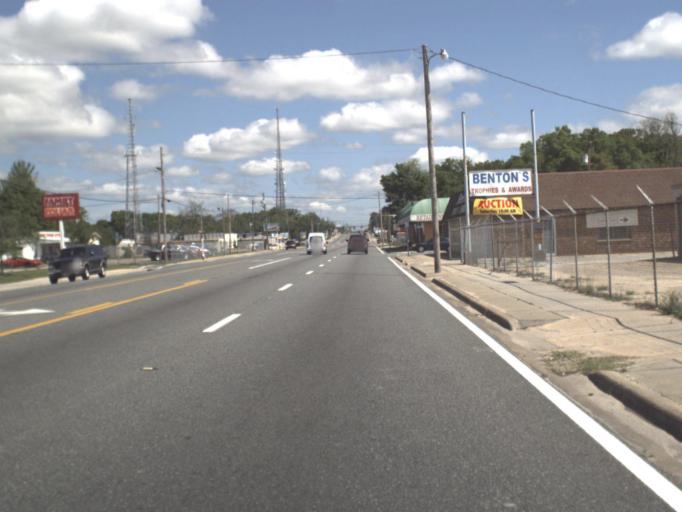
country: US
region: Florida
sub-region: Escambia County
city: Goulding
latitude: 30.4303
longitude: -87.2406
